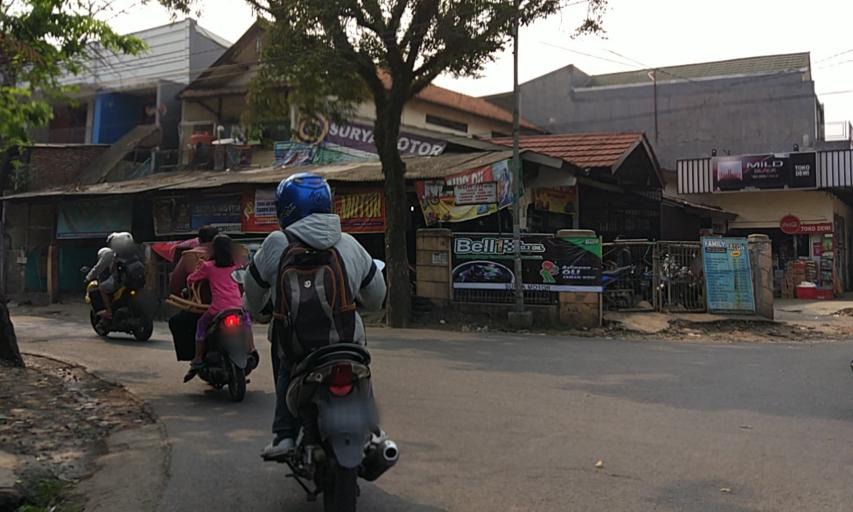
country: ID
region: West Java
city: Margahayukencana
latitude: -6.9493
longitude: 107.5654
